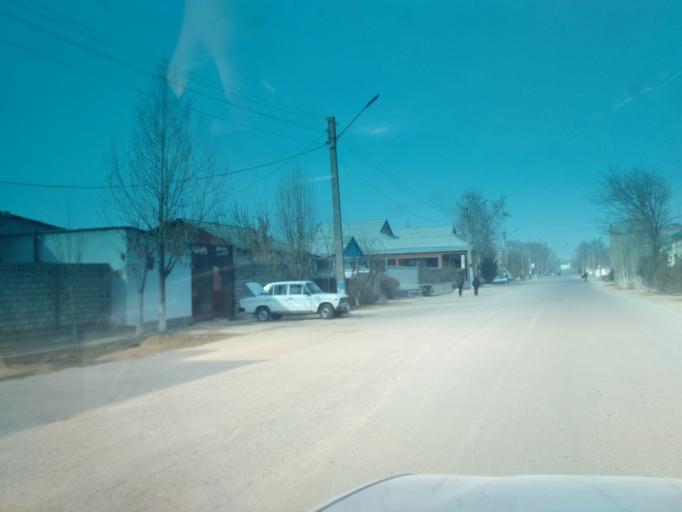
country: UZ
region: Sirdaryo
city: Guliston
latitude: 40.4934
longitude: 68.7833
